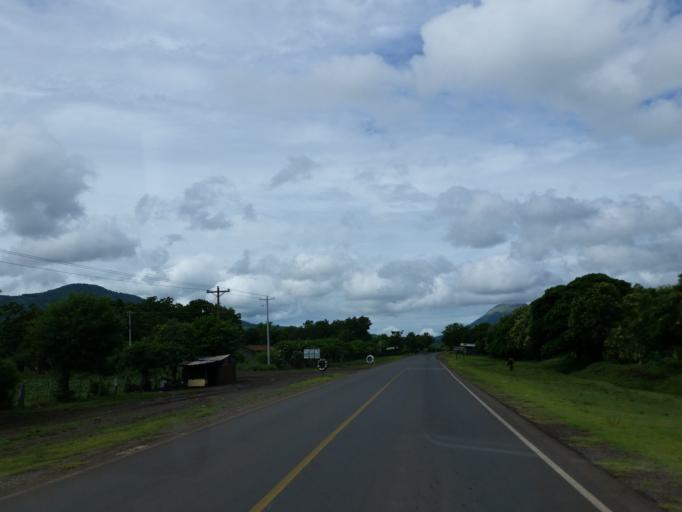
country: NI
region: Leon
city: Larreynaga
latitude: 12.5959
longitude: -86.7064
